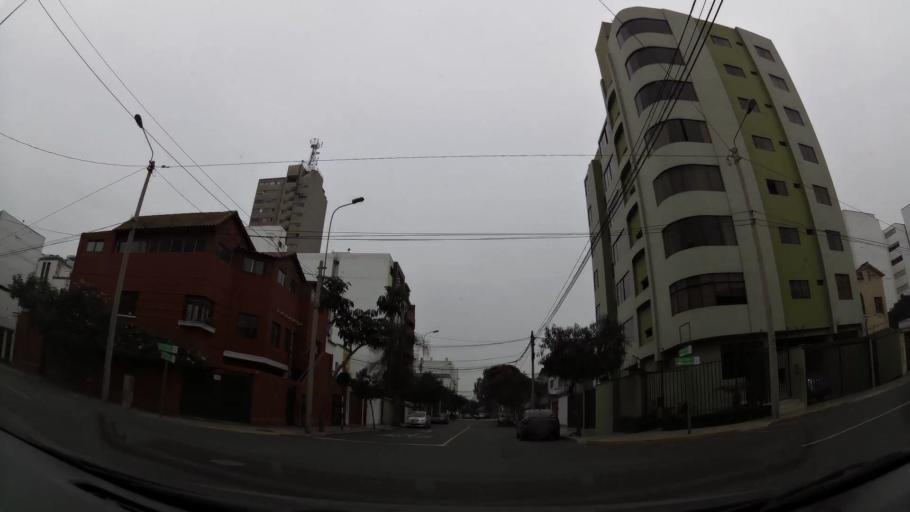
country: PE
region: Lima
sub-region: Lima
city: San Isidro
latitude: -12.1149
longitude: -77.0313
